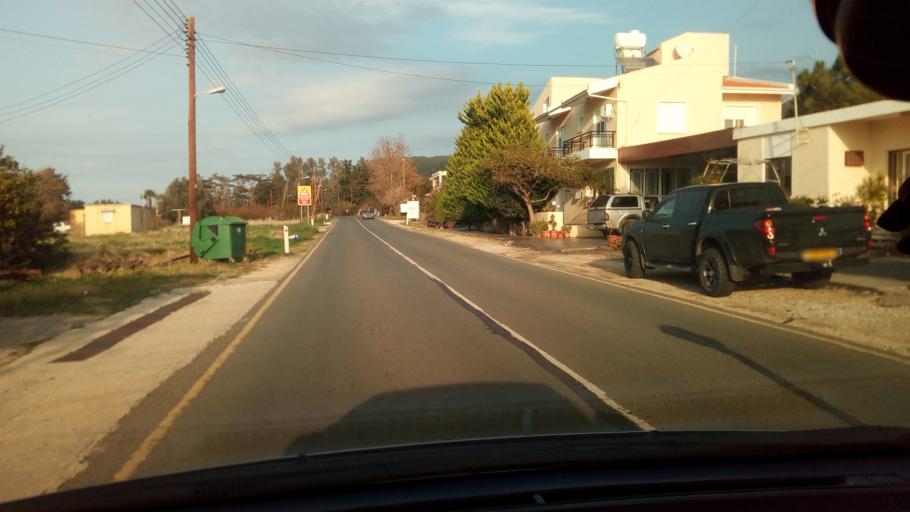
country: CY
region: Pafos
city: Polis
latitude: 35.1227
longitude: 32.5151
